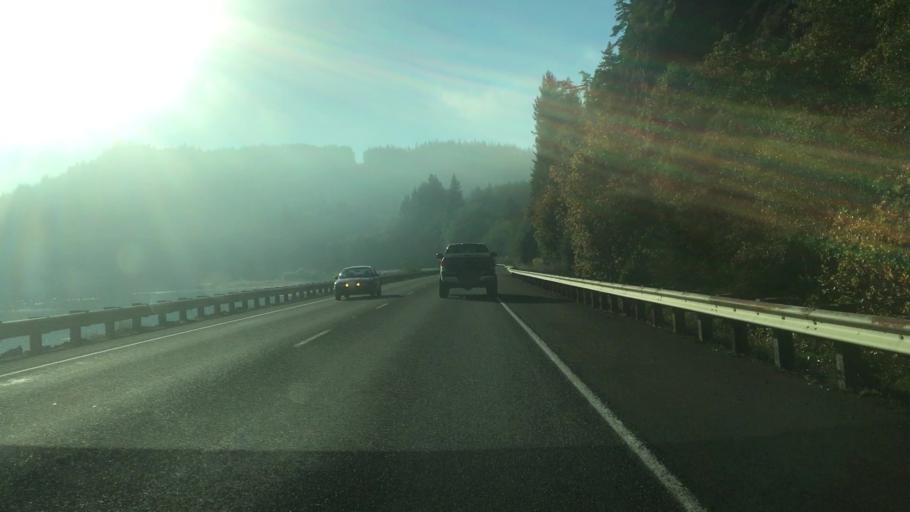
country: US
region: Oregon
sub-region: Clatsop County
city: Astoria
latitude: 46.2613
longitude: -123.8457
